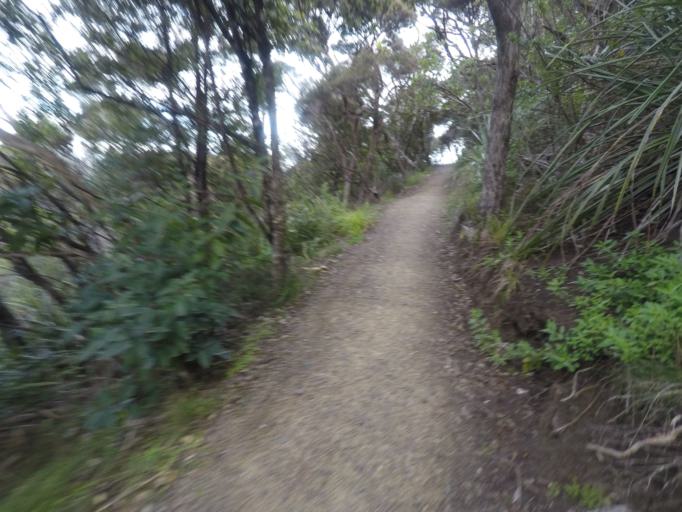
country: NZ
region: Auckland
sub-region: Auckland
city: Muriwai Beach
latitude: -36.9808
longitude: 174.4722
